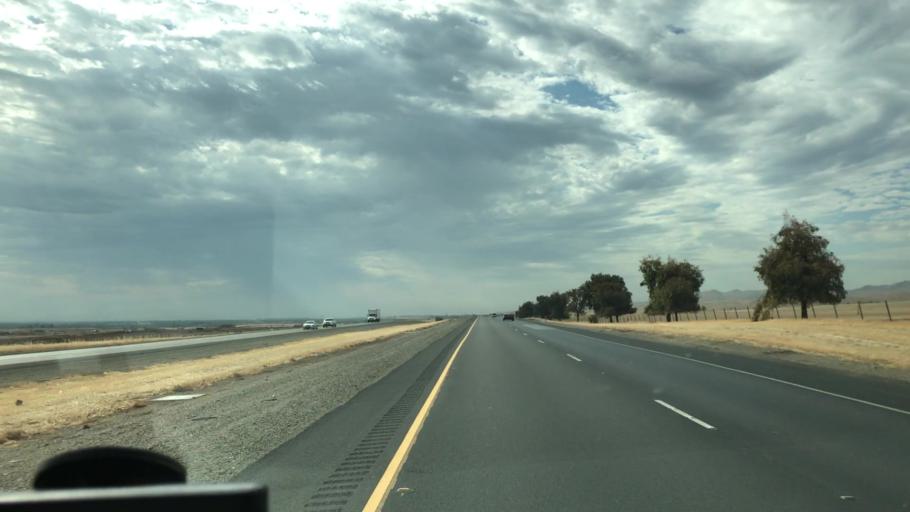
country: US
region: California
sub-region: San Joaquin County
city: Tracy
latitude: 37.6787
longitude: -121.4682
